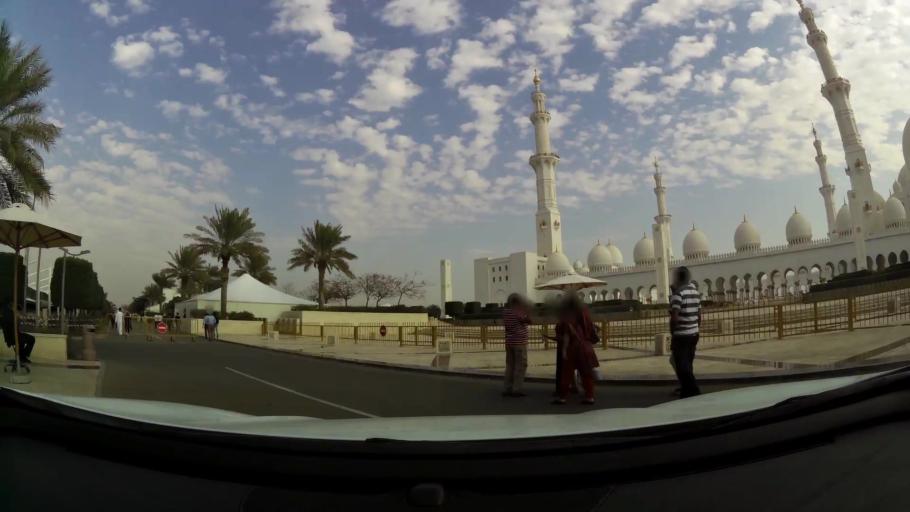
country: AE
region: Abu Dhabi
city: Abu Dhabi
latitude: 24.4143
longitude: 54.4745
